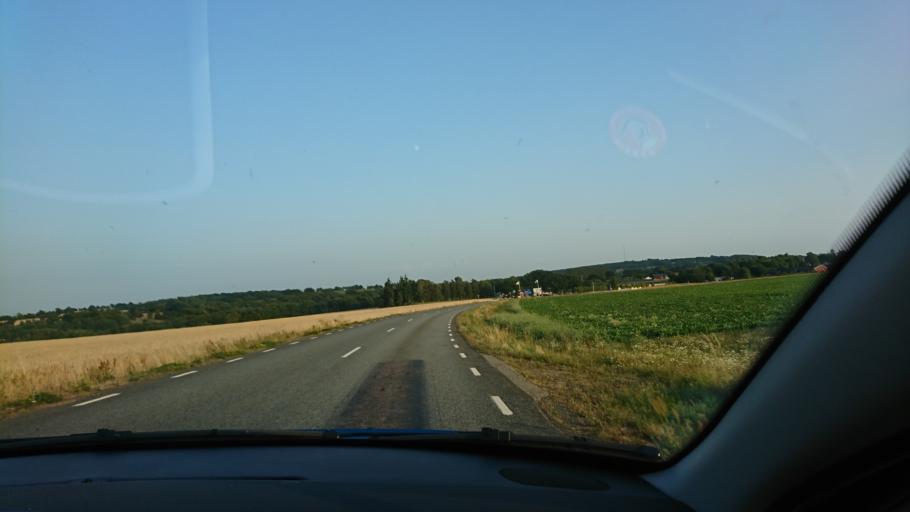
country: SE
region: Skane
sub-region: Simrishamns Kommun
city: Kivik
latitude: 55.6935
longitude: 14.1570
